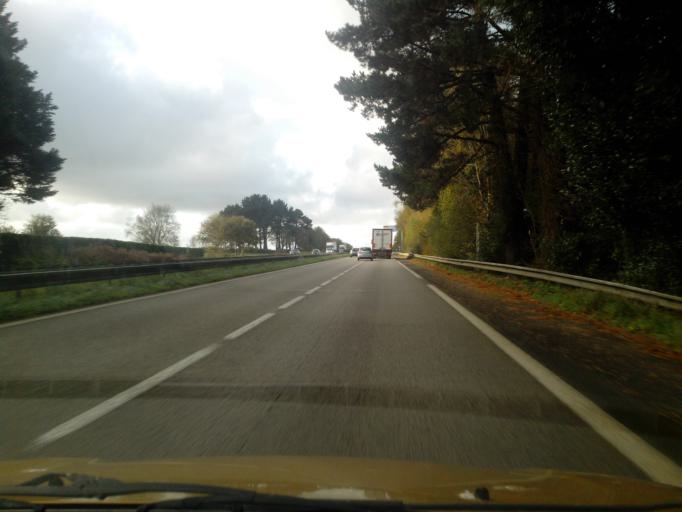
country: FR
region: Brittany
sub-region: Departement du Morbihan
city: Branderion
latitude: 47.8195
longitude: -3.2152
